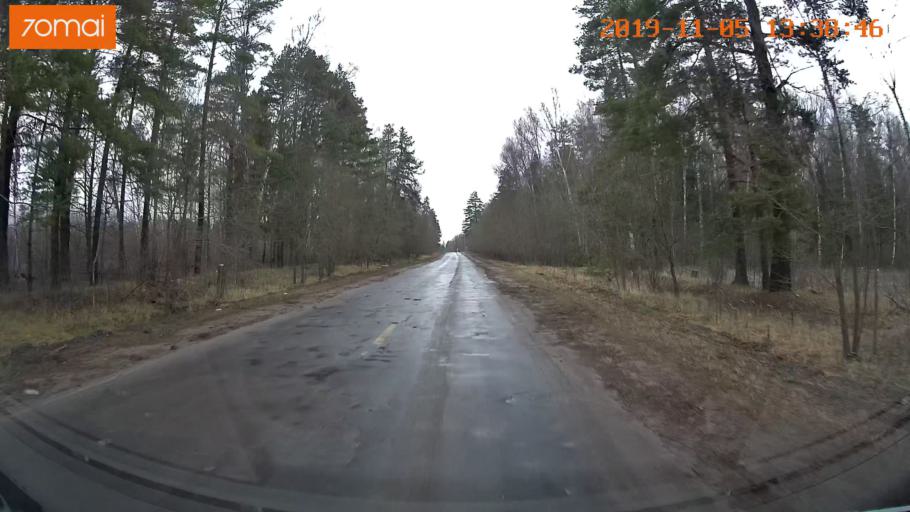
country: RU
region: Ivanovo
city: Shuya
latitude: 56.9345
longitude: 41.3869
